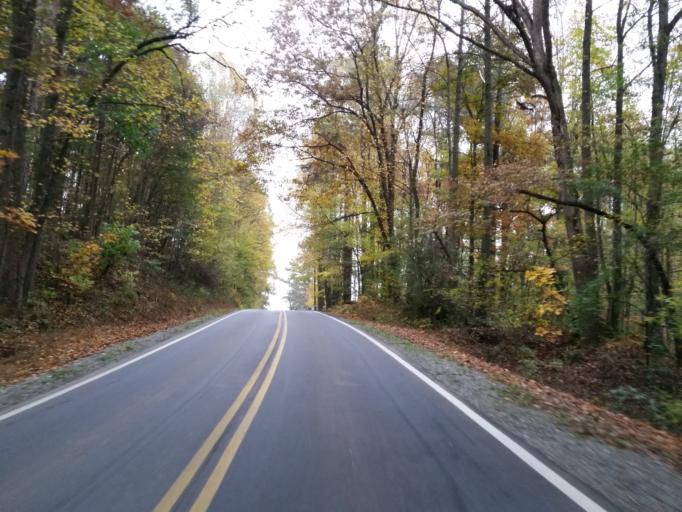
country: US
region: Georgia
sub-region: Gilmer County
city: Ellijay
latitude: 34.6508
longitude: -84.3507
